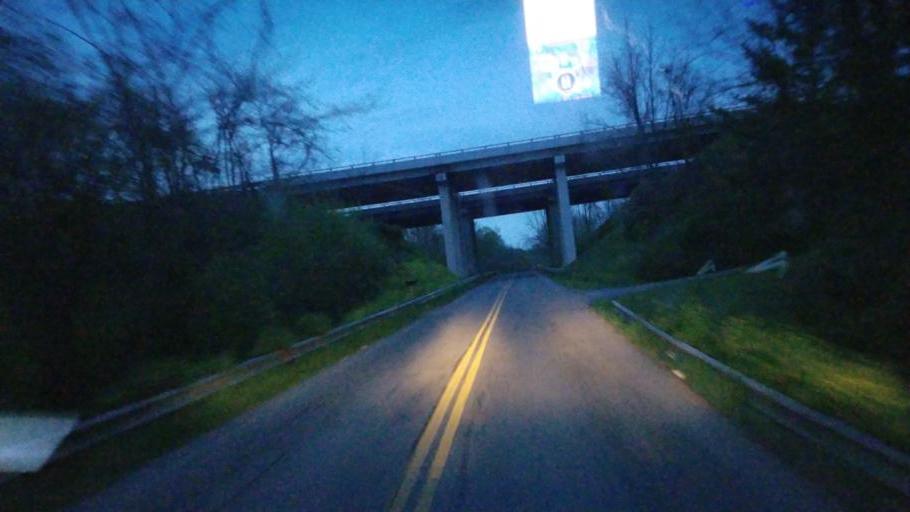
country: US
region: Virginia
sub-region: Smyth County
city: Atkins
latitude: 36.8544
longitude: -81.4679
